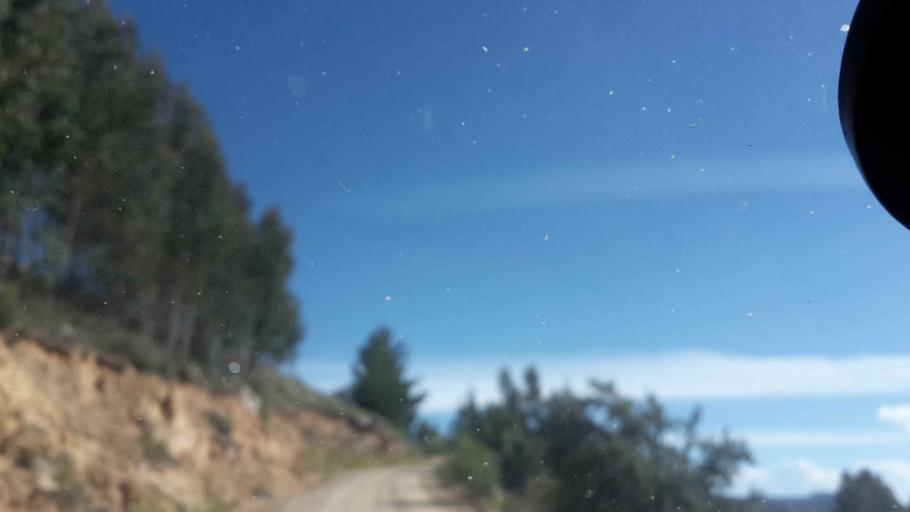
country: BO
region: Cochabamba
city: Arani
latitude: -17.6793
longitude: -65.7243
